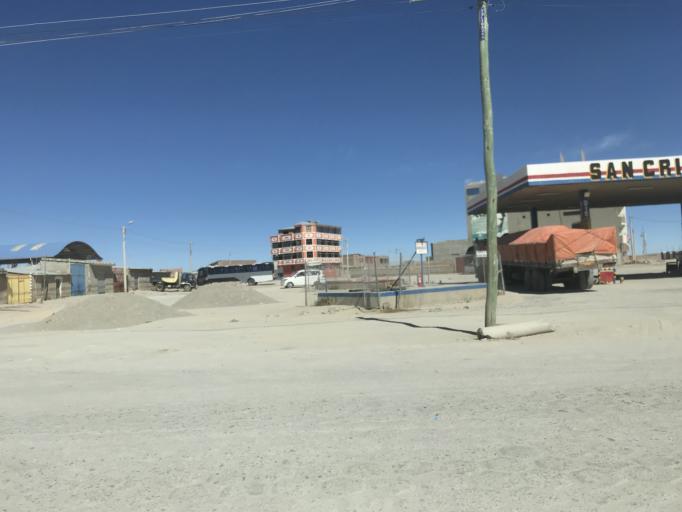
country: BO
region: Potosi
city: Uyuni
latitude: -20.4548
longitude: -66.8301
